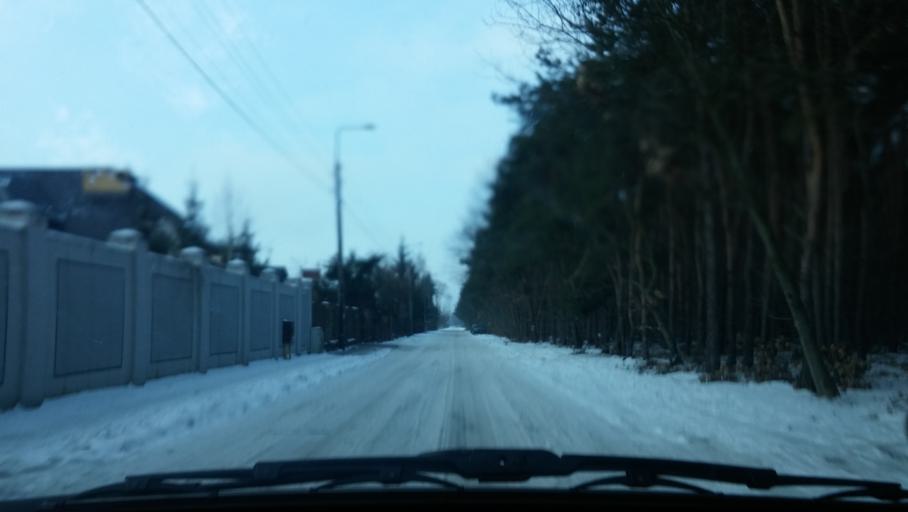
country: PL
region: Masovian Voivodeship
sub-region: Powiat otwocki
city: Jozefow
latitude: 52.1552
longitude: 21.2003
